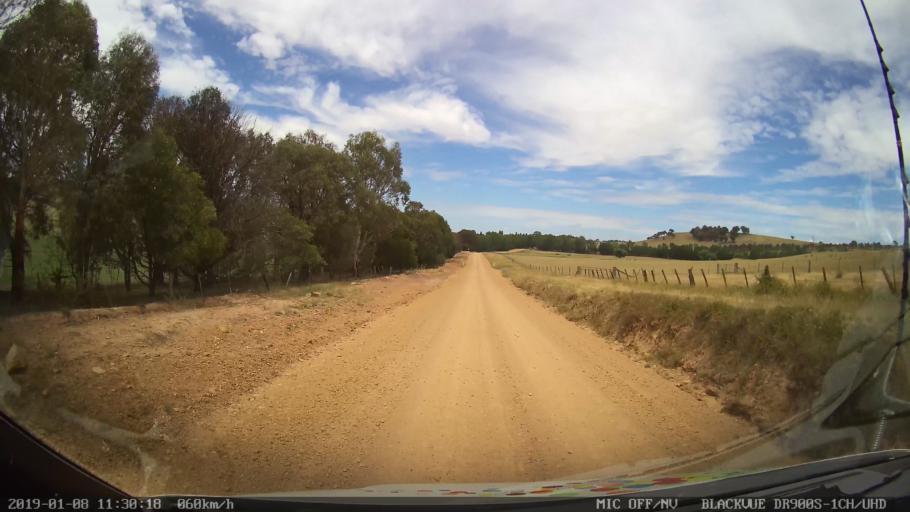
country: AU
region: New South Wales
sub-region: Guyra
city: Guyra
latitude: -30.3067
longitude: 151.5451
